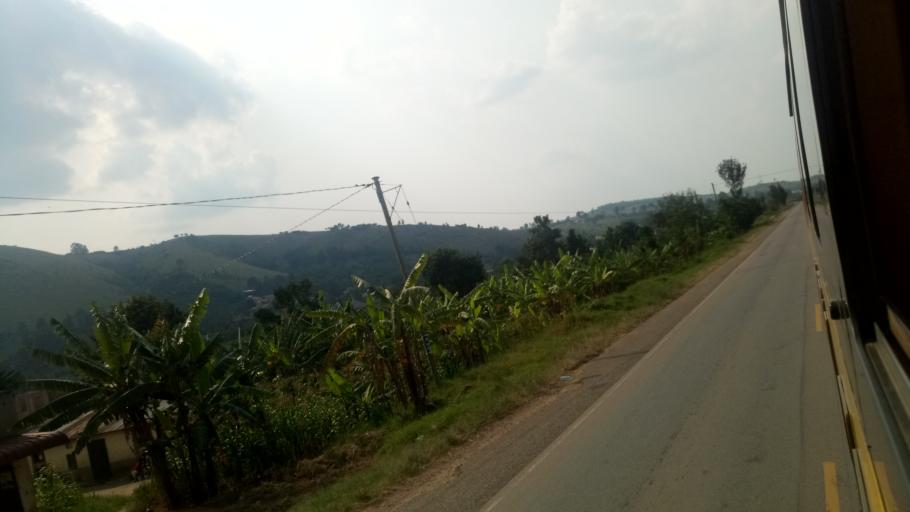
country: UG
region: Western Region
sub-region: Mbarara District
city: Mbarara
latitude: -0.5404
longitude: 30.7144
